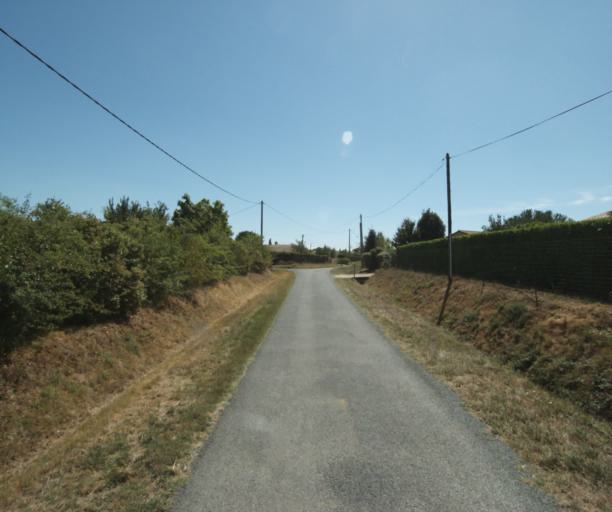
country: FR
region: Midi-Pyrenees
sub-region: Departement de la Haute-Garonne
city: Saint-Felix-Lauragais
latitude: 43.4827
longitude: 1.9173
